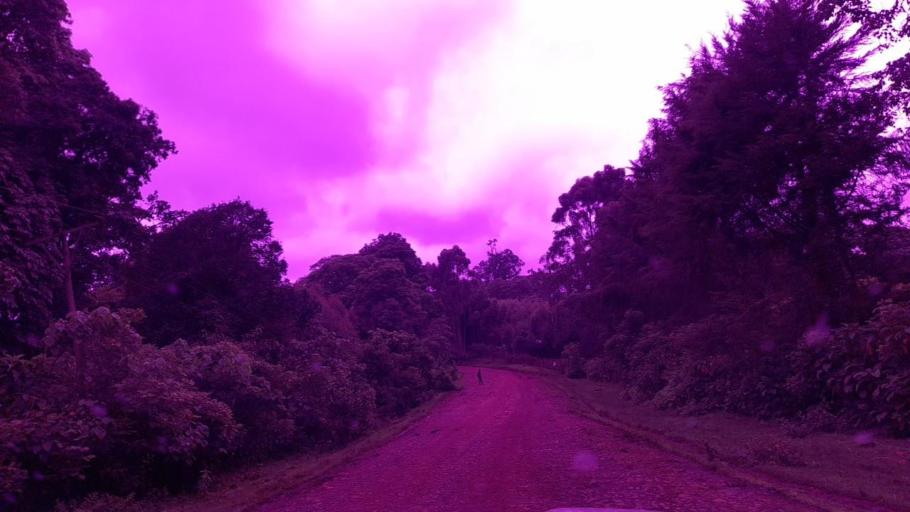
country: ET
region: Southern Nations, Nationalities, and People's Region
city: Tippi
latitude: 7.5772
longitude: 35.7790
